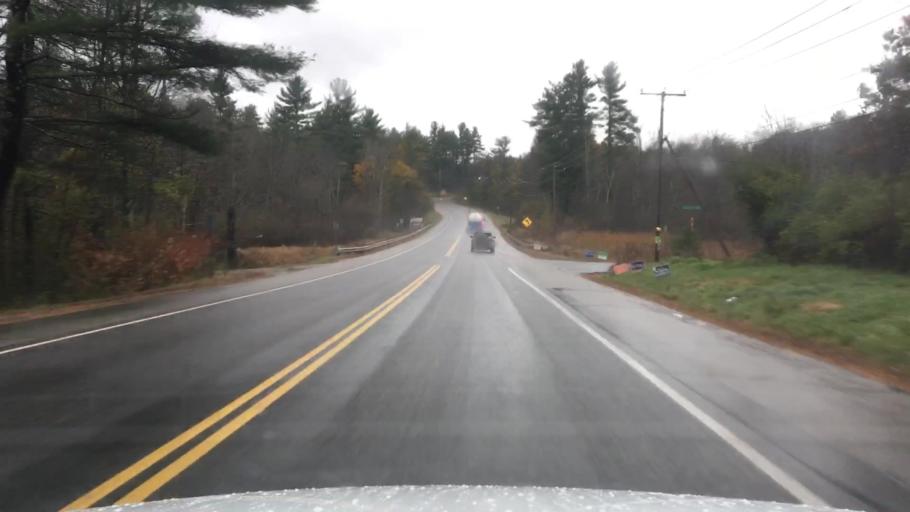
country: US
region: New Hampshire
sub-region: Strafford County
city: Barrington
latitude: 43.2343
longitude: -70.9919
